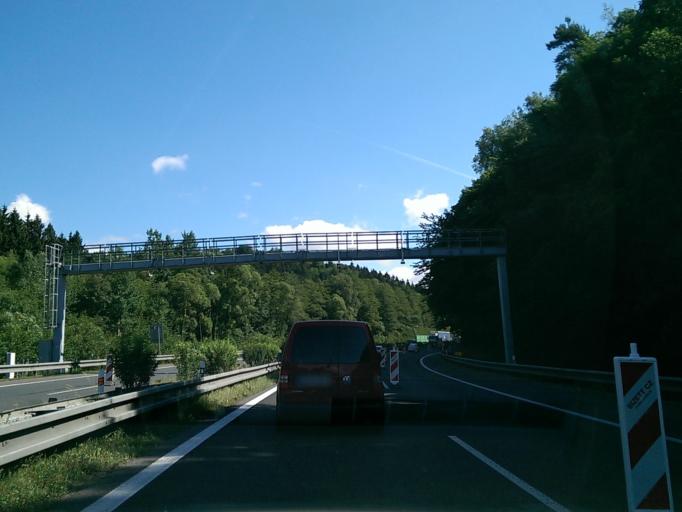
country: CZ
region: Liberecky
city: Hodkovice nad Mohelkou
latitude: 50.6734
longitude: 15.0957
